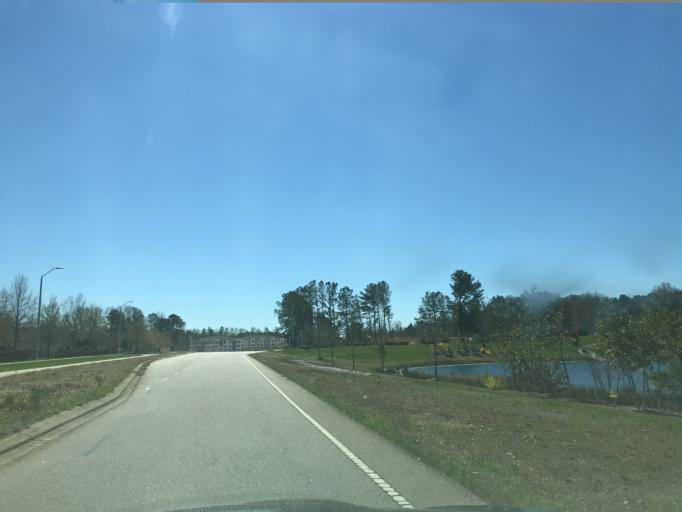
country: US
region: North Carolina
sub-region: Wake County
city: Garner
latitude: 35.6844
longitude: -78.5744
